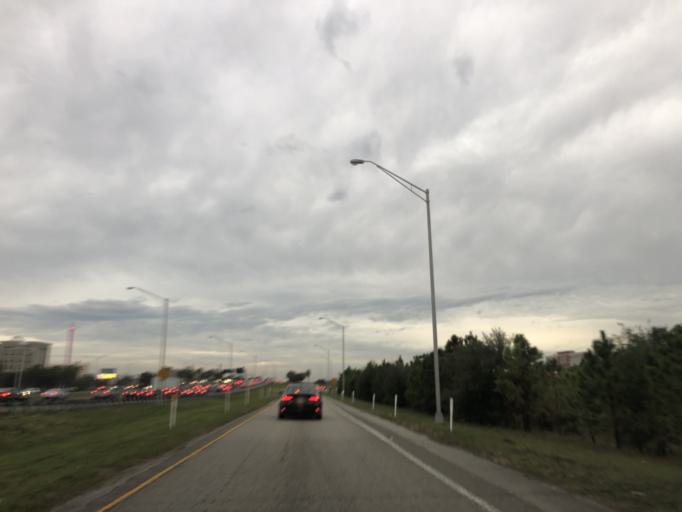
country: US
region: Florida
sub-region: Orange County
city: Doctor Phillips
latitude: 28.4552
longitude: -81.4749
